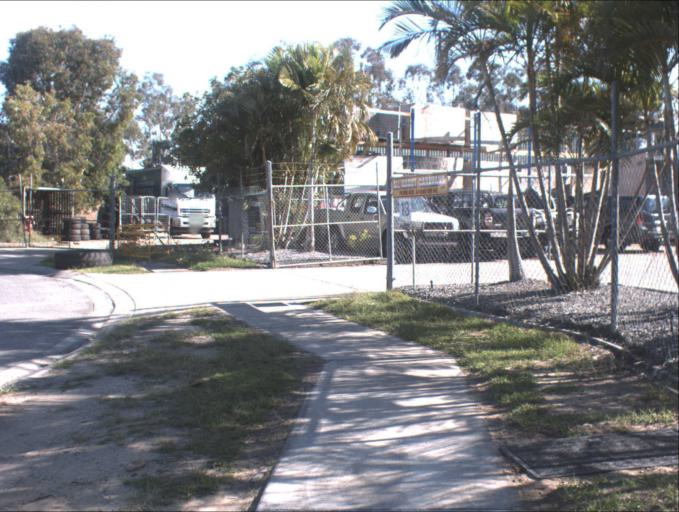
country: AU
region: Queensland
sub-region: Logan
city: Waterford West
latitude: -27.7036
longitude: 153.1556
